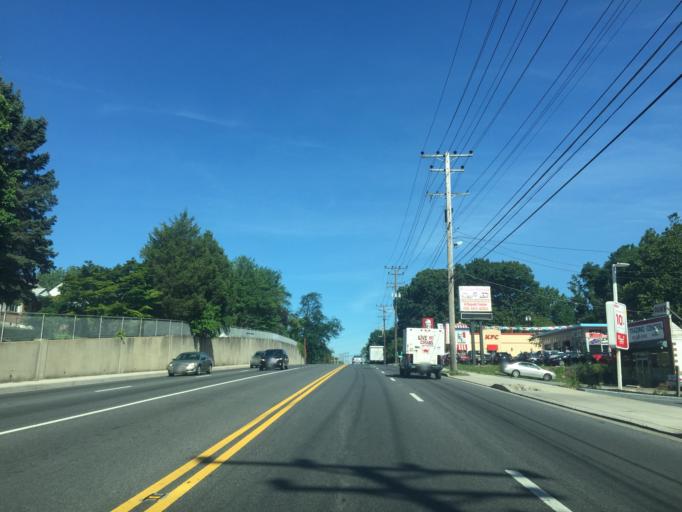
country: US
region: Maryland
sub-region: Baltimore County
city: Lochearn
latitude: 39.3454
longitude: -76.7348
